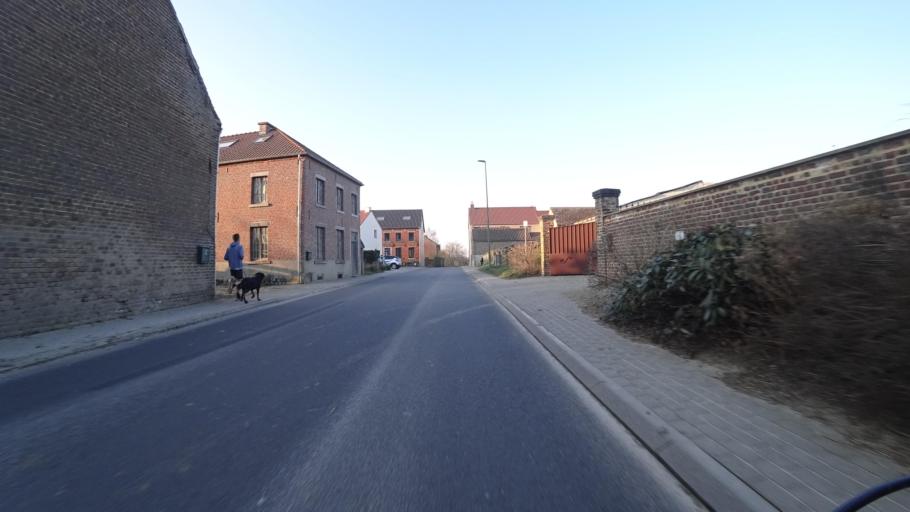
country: BE
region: Wallonia
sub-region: Province du Brabant Wallon
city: Chastre
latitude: 50.5915
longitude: 4.6416
